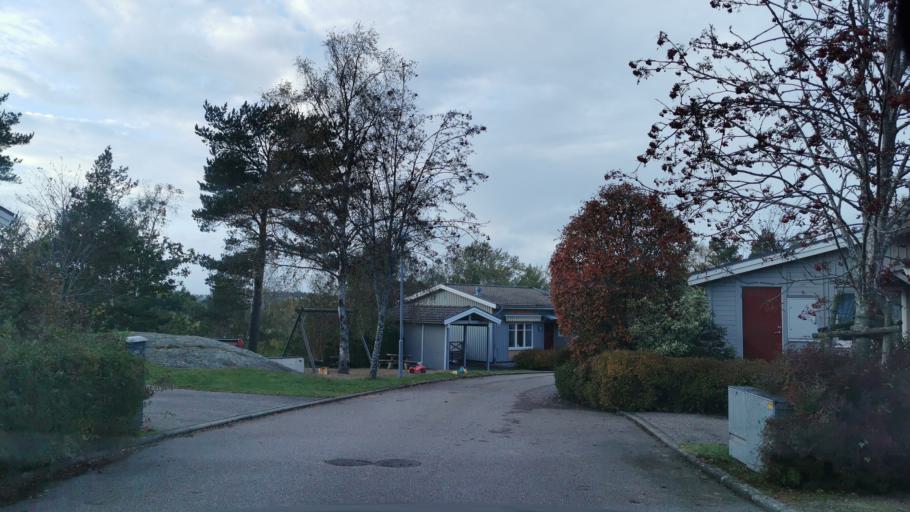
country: SE
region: Vaestra Goetaland
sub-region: Partille Kommun
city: Partille
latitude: 57.7138
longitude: 12.0832
